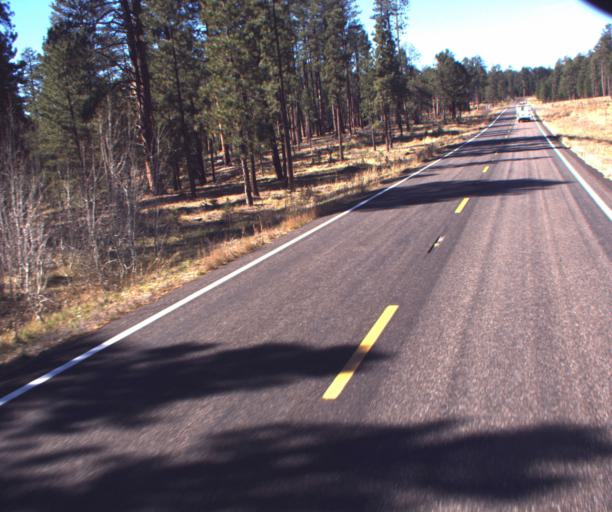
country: US
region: Arizona
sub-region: Coconino County
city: Fredonia
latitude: 36.6812
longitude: -112.2139
